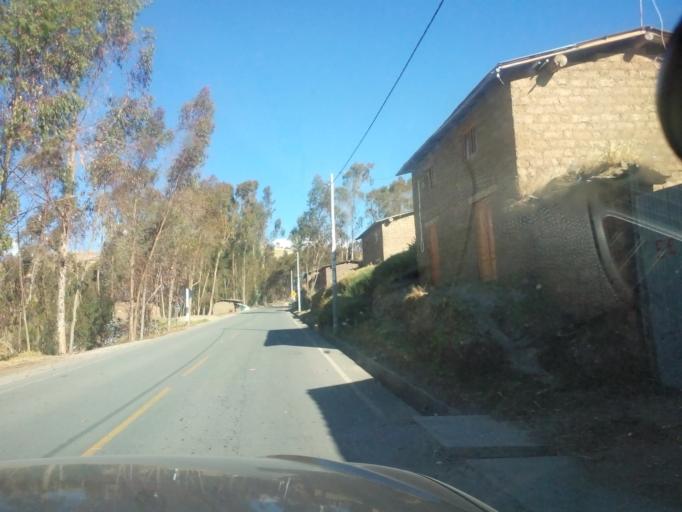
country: PE
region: Apurimac
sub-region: Provincia de Andahuaylas
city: Pacucha
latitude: -13.6519
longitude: -73.2948
